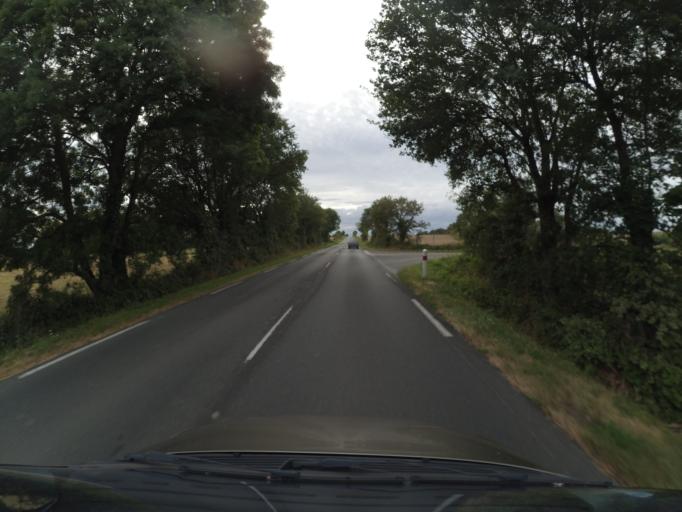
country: FR
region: Pays de la Loire
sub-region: Departement de la Vendee
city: Mortagne-sur-Sevre
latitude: 47.0113
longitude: -0.9845
